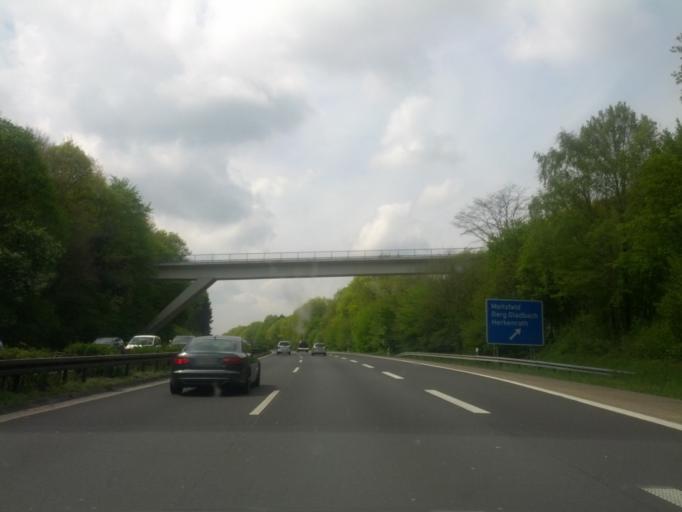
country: DE
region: North Rhine-Westphalia
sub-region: Regierungsbezirk Koln
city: Bergisch Gladbach
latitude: 50.9569
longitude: 7.1868
